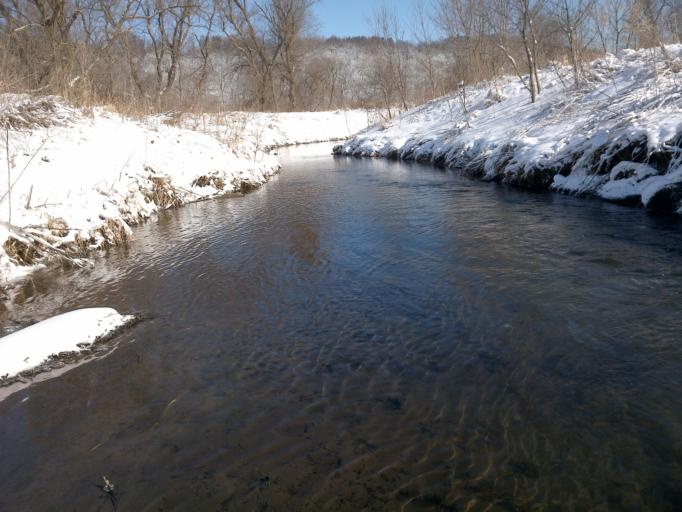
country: US
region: Minnesota
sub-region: Goodhue County
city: Goodhue
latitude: 44.4762
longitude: -92.5879
